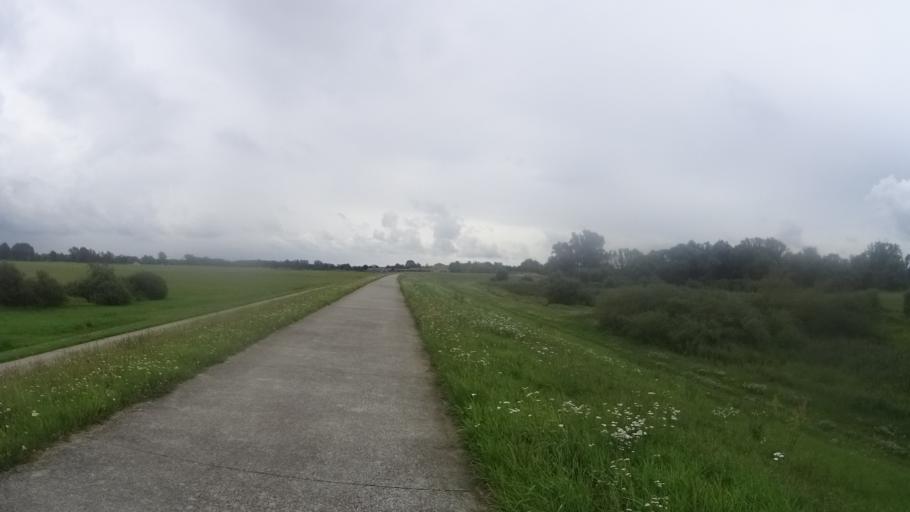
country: DE
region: Lower Saxony
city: Bleckede
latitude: 53.2961
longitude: 10.7915
